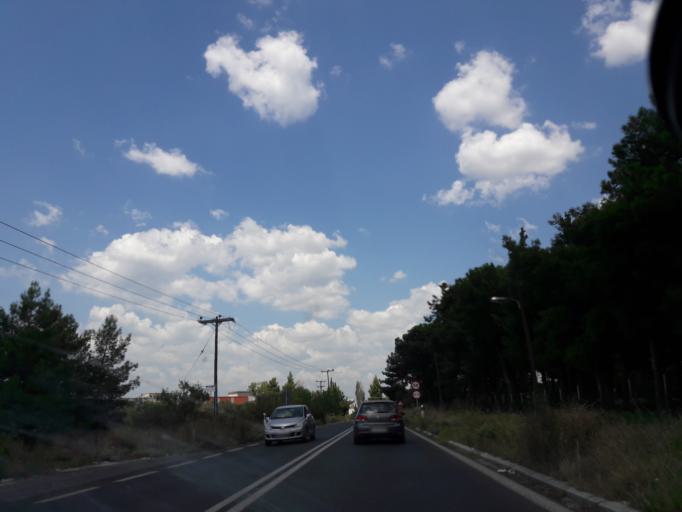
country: GR
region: Central Macedonia
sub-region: Nomos Thessalonikis
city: Thermi
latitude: 40.5368
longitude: 23.0359
